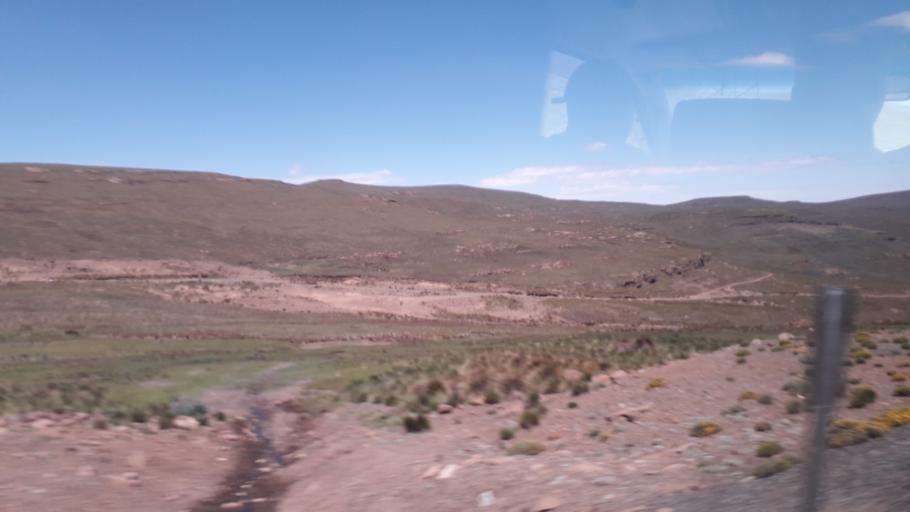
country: ZA
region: Orange Free State
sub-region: Thabo Mofutsanyana District Municipality
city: Phuthaditjhaba
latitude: -28.8120
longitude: 28.7138
